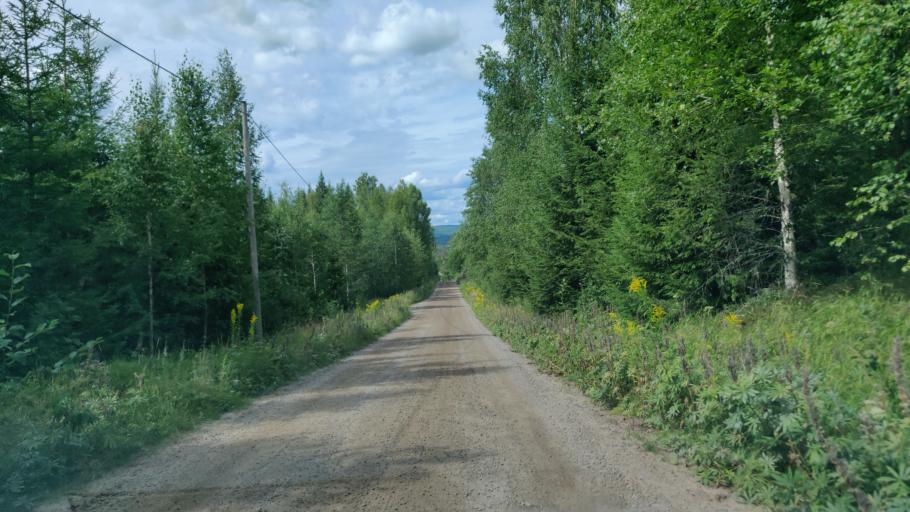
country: SE
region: Vaermland
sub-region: Hagfors Kommun
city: Hagfors
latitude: 60.0182
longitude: 13.7018
